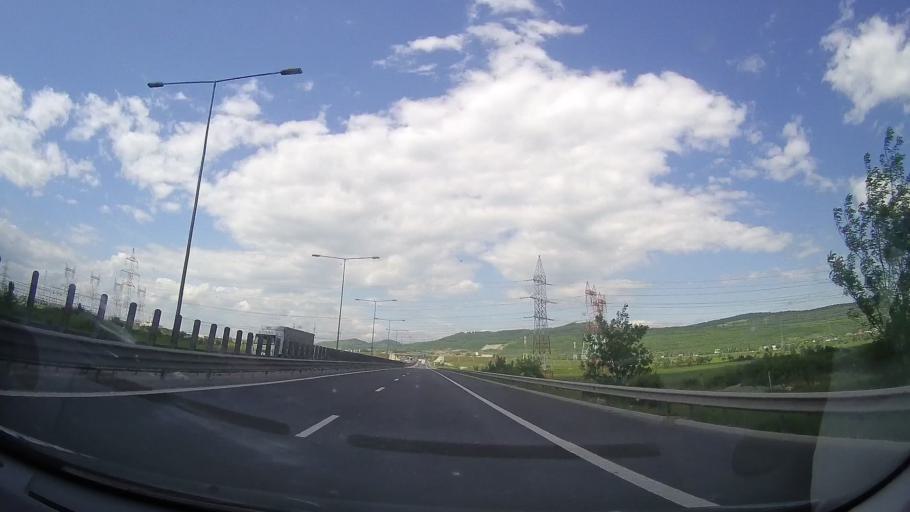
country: RO
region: Sibiu
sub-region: Comuna Selimbar
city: Selimbar
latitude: 45.7840
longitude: 24.2009
